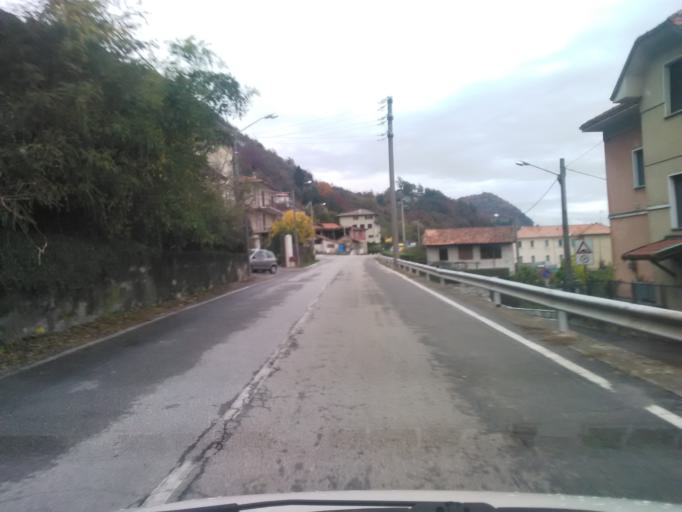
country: IT
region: Piedmont
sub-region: Provincia Verbano-Cusio-Ossola
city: Madonna del Sasso
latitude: 45.7916
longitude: 8.3776
